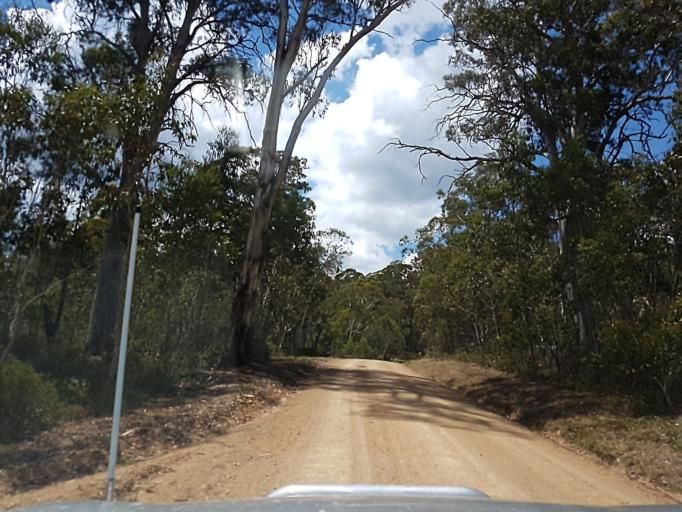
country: AU
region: New South Wales
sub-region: Snowy River
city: Jindabyne
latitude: -36.8780
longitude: 148.0759
